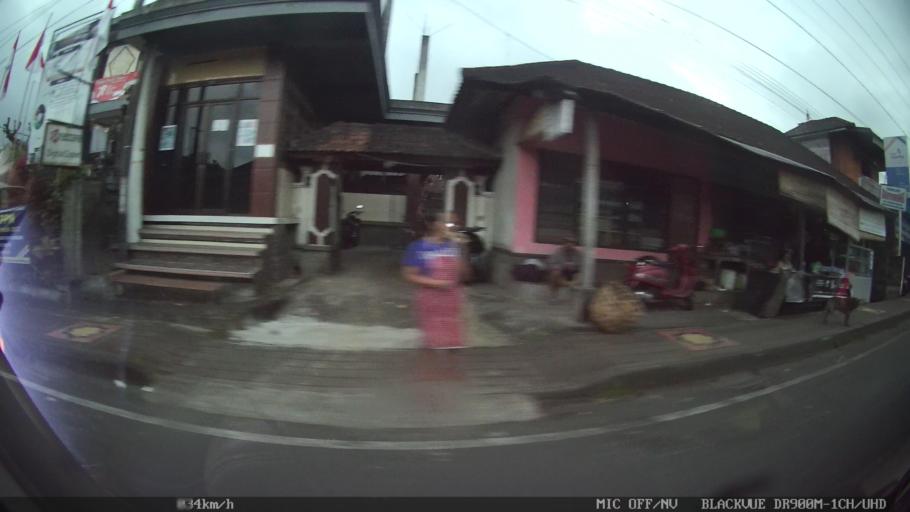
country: ID
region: Bali
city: Badung
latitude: -8.4355
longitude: 115.2449
